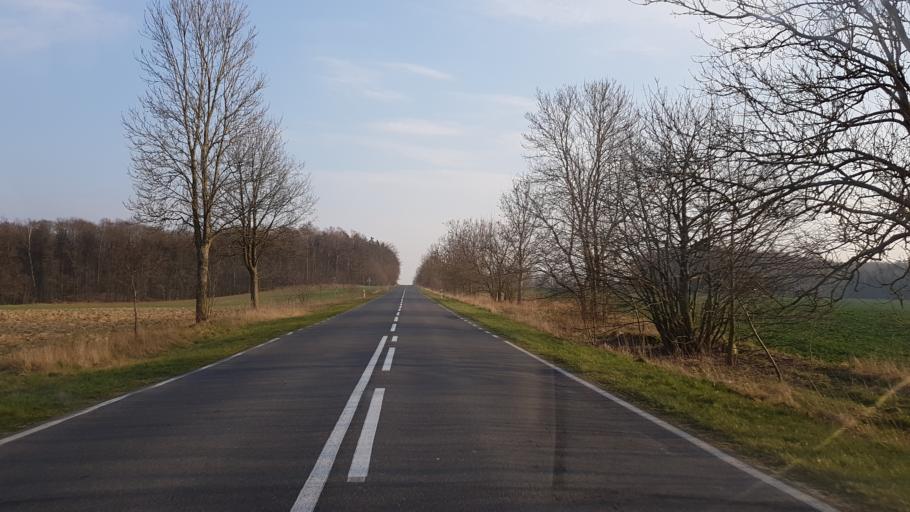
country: PL
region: West Pomeranian Voivodeship
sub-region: Powiat swidwinski
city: Slawoborze
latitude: 53.8475
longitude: 15.7357
